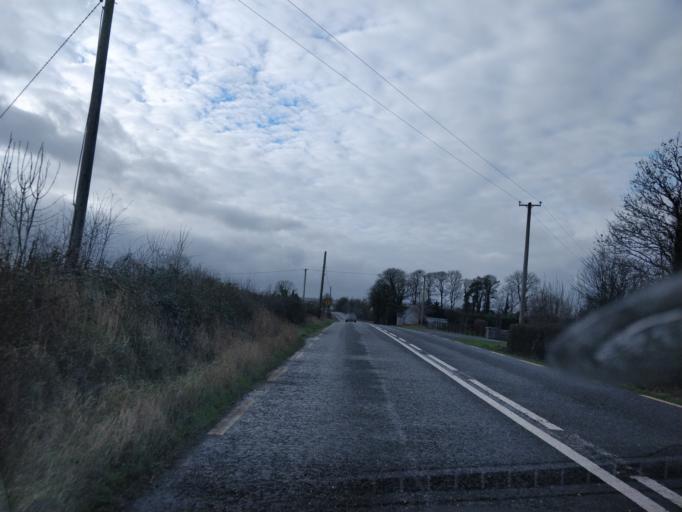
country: IE
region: Connaught
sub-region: Roscommon
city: Roscommon
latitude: 53.7684
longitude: -8.1619
